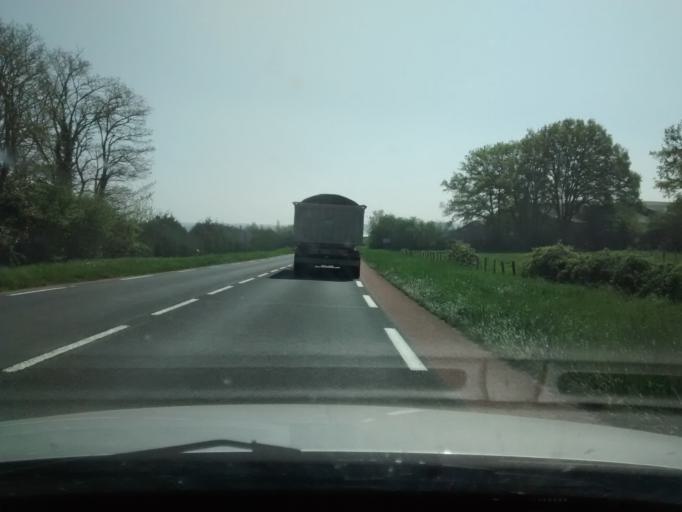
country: FR
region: Pays de la Loire
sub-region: Departement de la Sarthe
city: Loue
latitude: 48.0226
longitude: -0.0873
